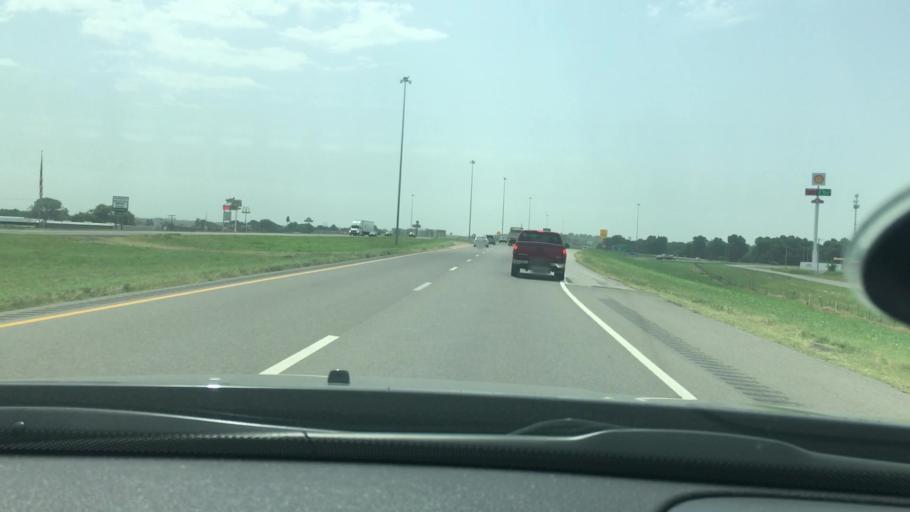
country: US
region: Oklahoma
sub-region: Garvin County
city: Pauls Valley
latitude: 34.7437
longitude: -97.2674
